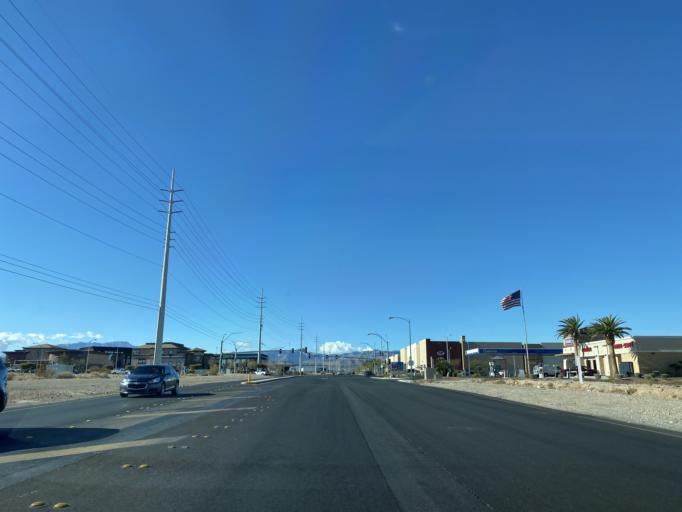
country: US
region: Nevada
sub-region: Clark County
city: Spring Valley
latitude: 36.0710
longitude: -115.2225
